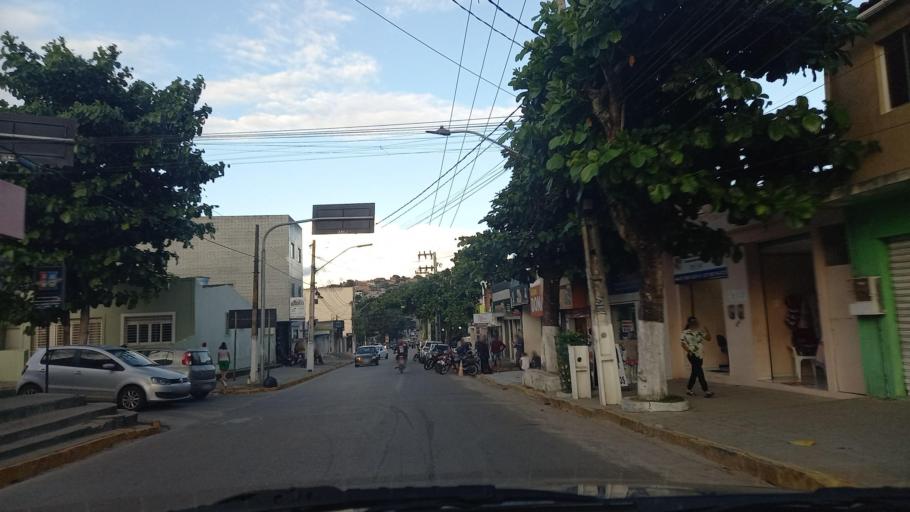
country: BR
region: Pernambuco
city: Garanhuns
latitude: -8.8851
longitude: -36.4667
